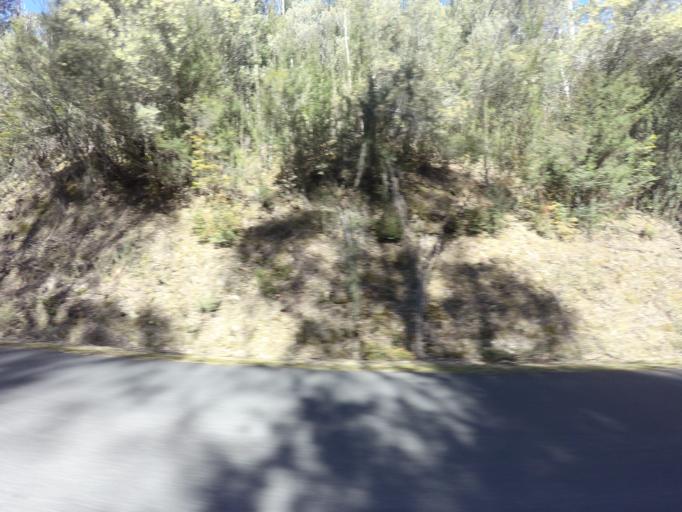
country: AU
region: Tasmania
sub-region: Derwent Valley
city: New Norfolk
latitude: -42.7237
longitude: 146.4352
